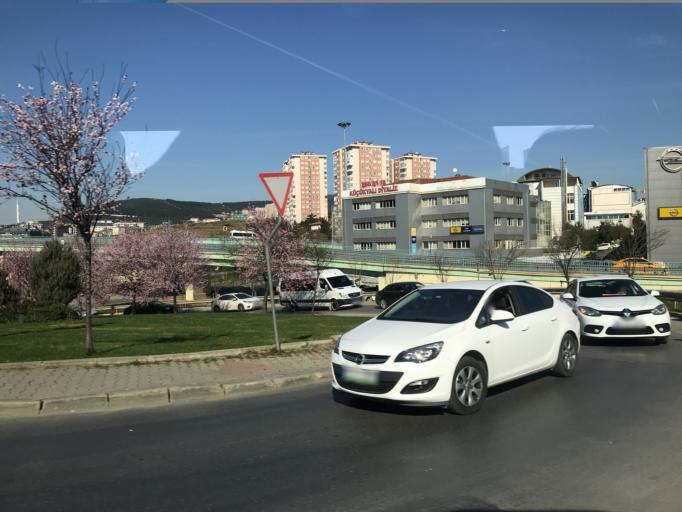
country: TR
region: Istanbul
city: Maltepe
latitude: 40.9428
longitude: 29.1307
